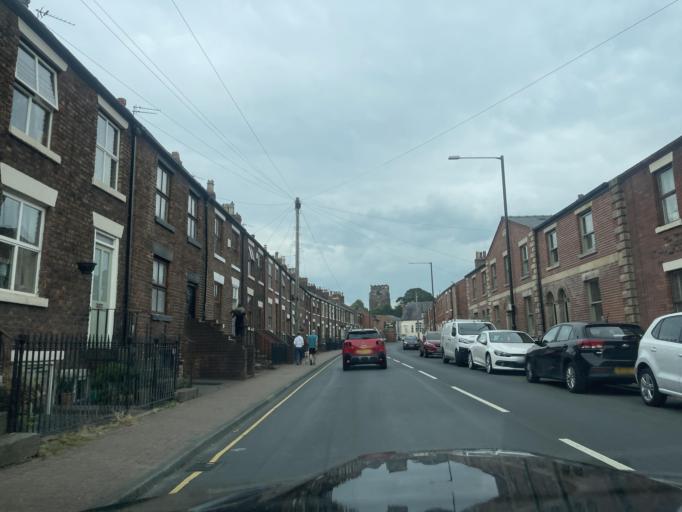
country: GB
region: England
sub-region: Lancashire
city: Leyland
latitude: 53.6883
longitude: -2.7005
